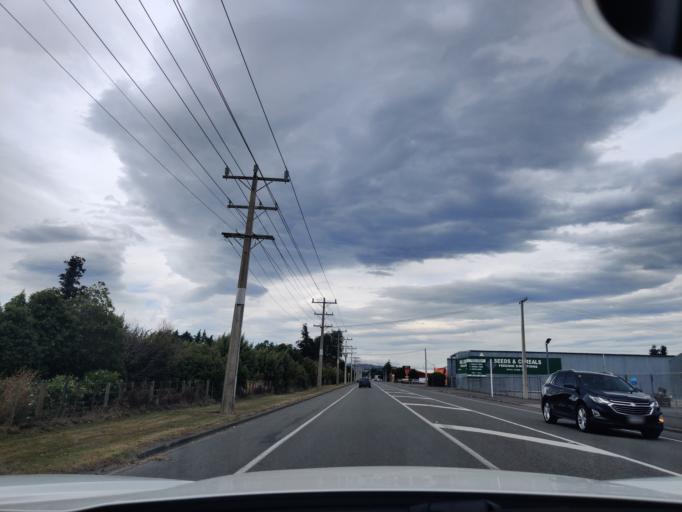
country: NZ
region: Wellington
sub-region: Masterton District
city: Masterton
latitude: -40.9491
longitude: 175.6331
